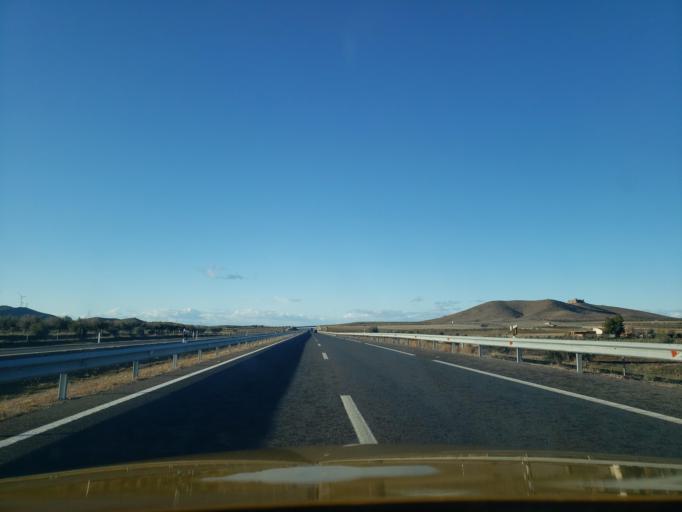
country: ES
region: Castille-La Mancha
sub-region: Province of Toledo
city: Villaminaya
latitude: 39.7264
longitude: -3.8484
